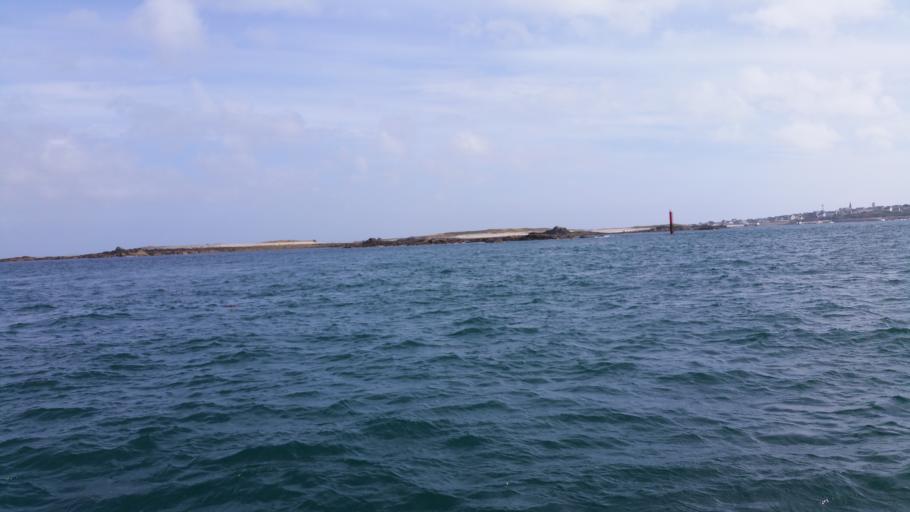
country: FR
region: Brittany
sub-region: Departement du Finistere
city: Le Conquet
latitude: 48.4117
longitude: -4.9501
